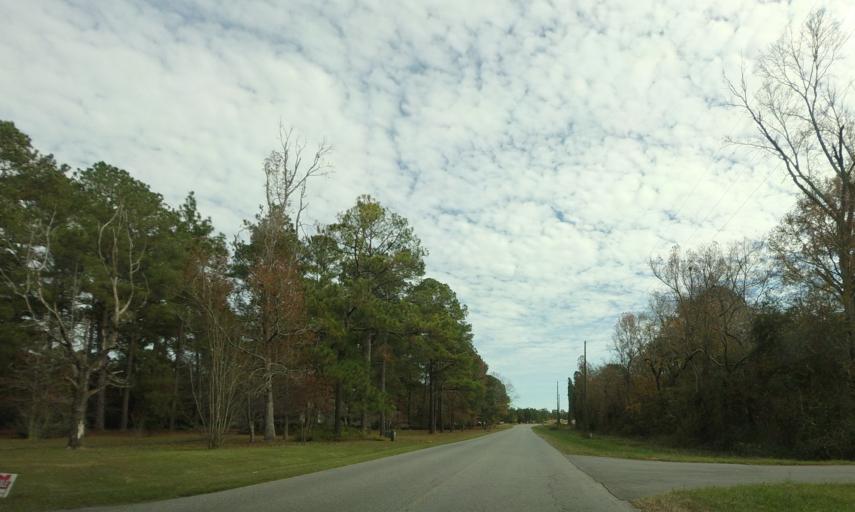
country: US
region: Georgia
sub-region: Bleckley County
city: Cochran
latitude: 32.3838
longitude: -83.3316
